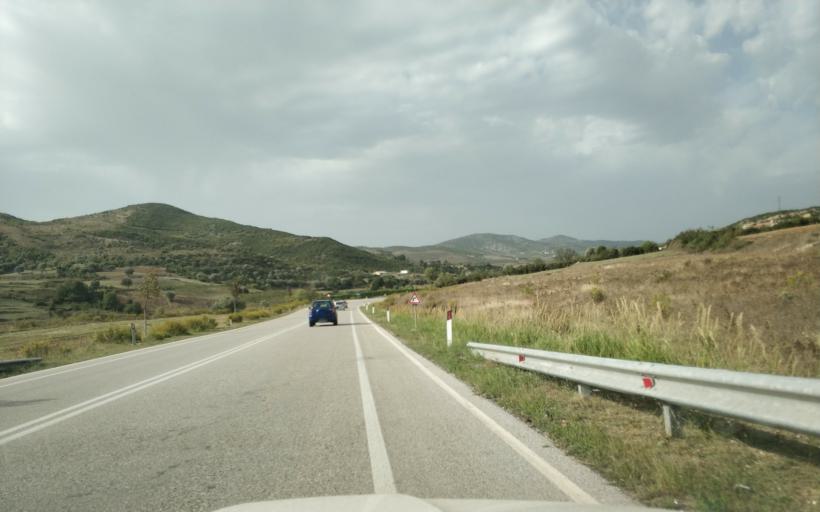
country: AL
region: Gjirokaster
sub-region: Rrethi i Tepelenes
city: Krahes
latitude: 40.4040
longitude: 19.8622
